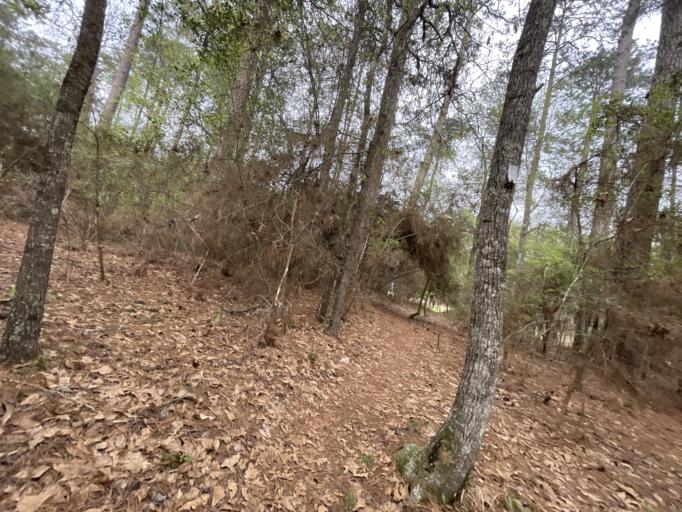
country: US
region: Texas
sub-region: Walker County
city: Huntsville
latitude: 30.6607
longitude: -95.4906
